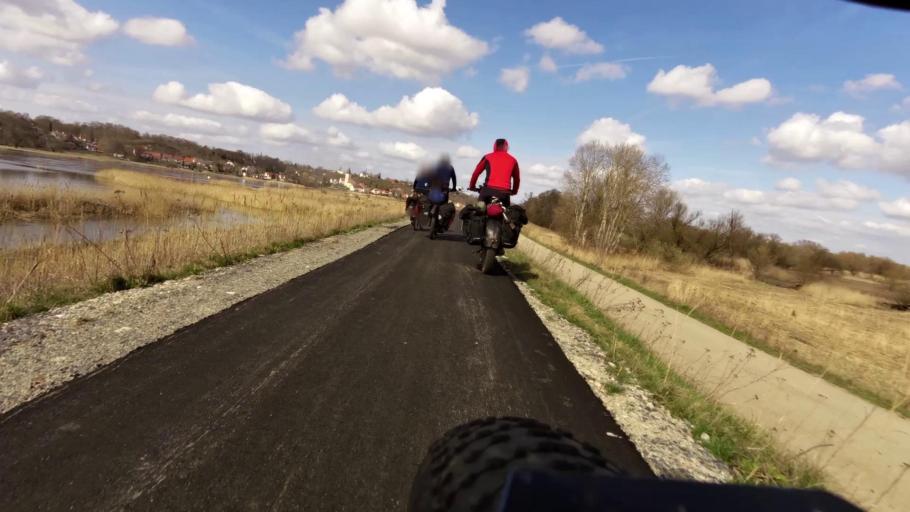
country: DE
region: Brandenburg
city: Lebus
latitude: 52.4190
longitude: 14.5483
